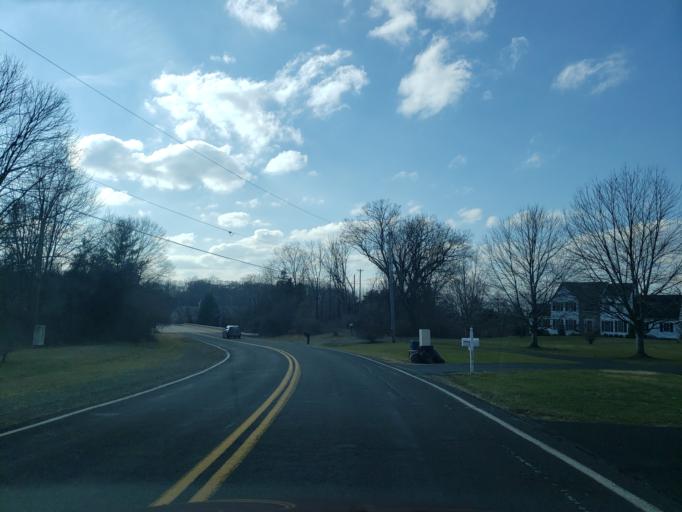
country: US
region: Pennsylvania
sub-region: Bucks County
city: Doylestown
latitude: 40.2916
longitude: -75.1316
